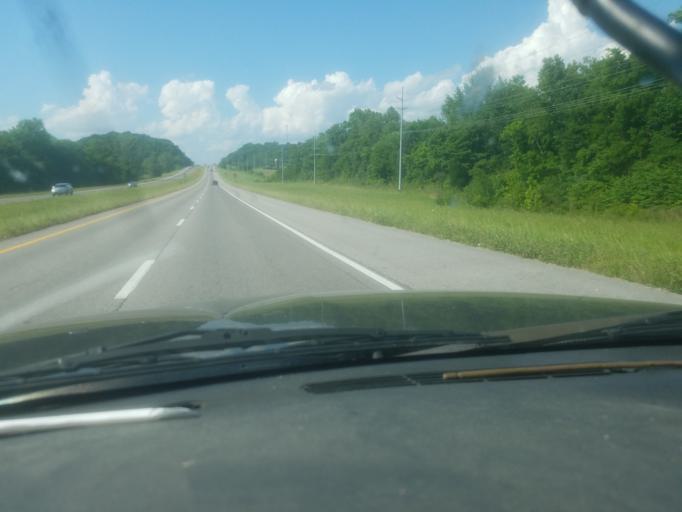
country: US
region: Tennessee
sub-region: Maury County
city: Mount Pleasant
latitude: 35.5259
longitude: -87.2222
